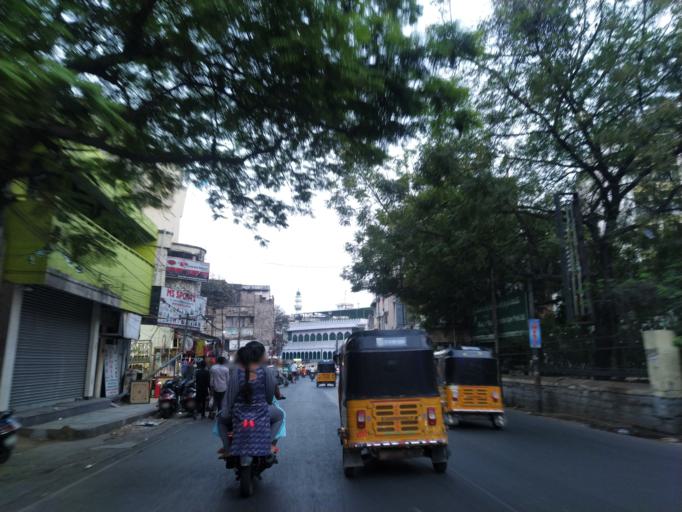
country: IN
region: Telangana
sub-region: Hyderabad
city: Hyderabad
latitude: 17.3864
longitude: 78.4787
